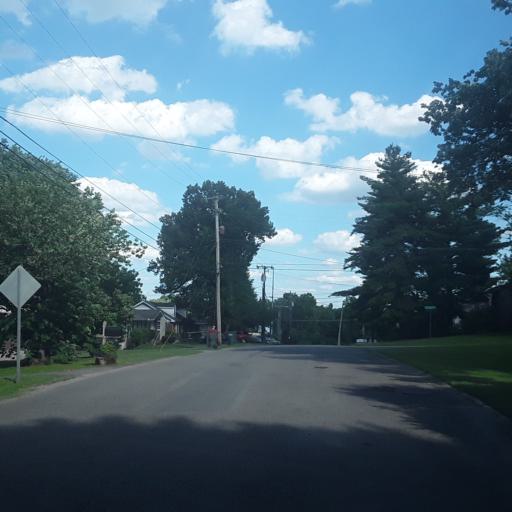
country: US
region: Tennessee
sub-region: Davidson County
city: Lakewood
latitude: 36.1932
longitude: -86.6273
